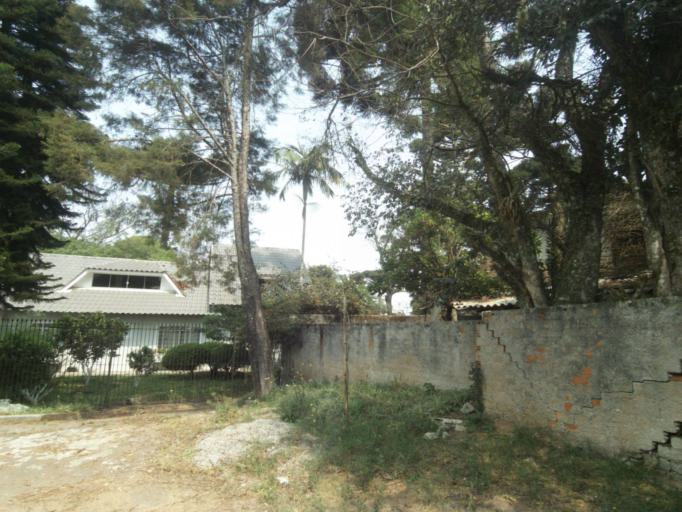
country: BR
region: Parana
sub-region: Pinhais
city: Pinhais
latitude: -25.4846
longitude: -49.2122
